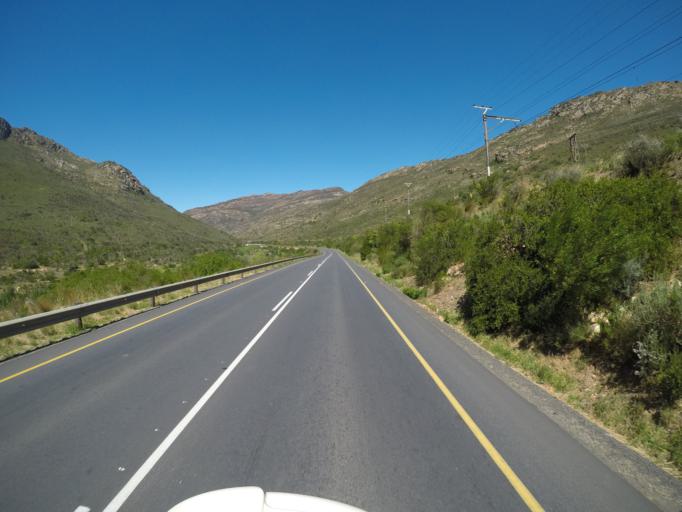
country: ZA
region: Western Cape
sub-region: Cape Winelands District Municipality
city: Ceres
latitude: -33.3061
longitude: 19.0695
